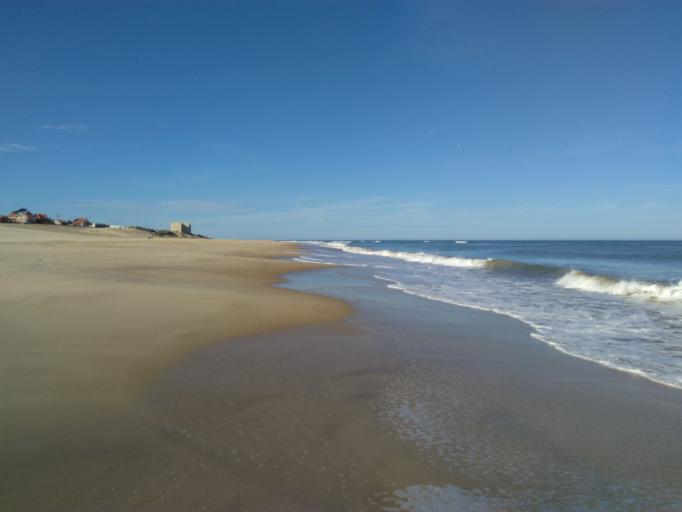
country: FR
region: Aquitaine
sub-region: Departement de la Gironde
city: Soulac-sur-Mer
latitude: 45.5184
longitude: -1.1277
